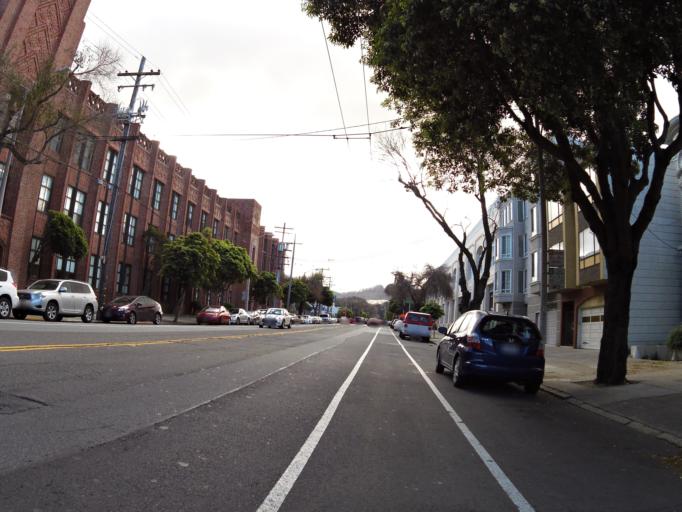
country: US
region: California
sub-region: San Francisco County
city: San Francisco
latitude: 37.7827
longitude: -122.4591
